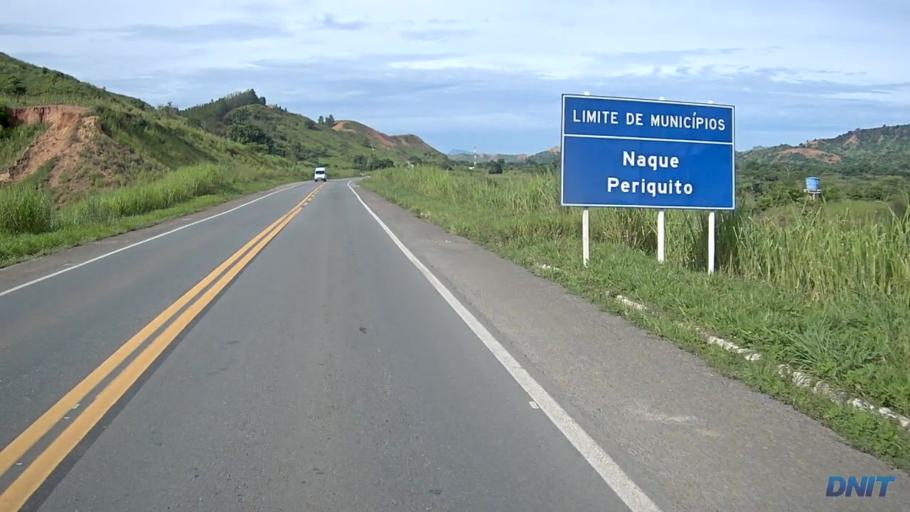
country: BR
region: Minas Gerais
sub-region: Belo Oriente
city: Belo Oriente
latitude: -19.1836
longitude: -42.2633
